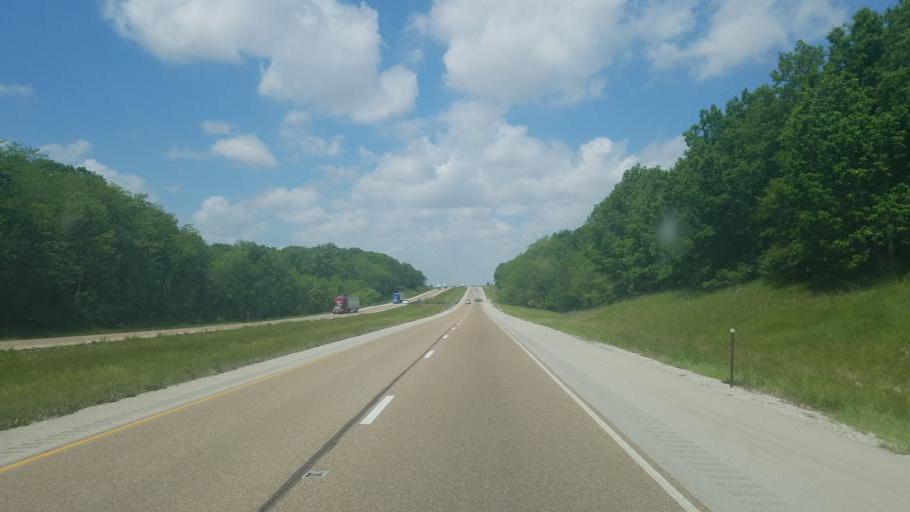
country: US
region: Illinois
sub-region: Clark County
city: Casey
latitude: 39.2826
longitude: -88.0600
